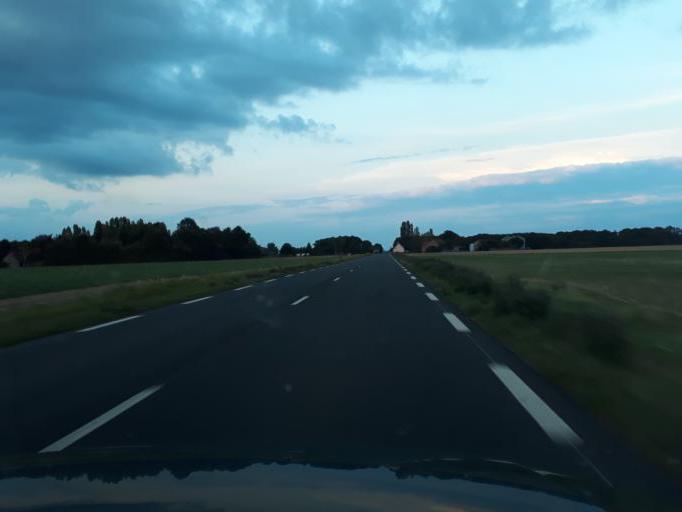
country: FR
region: Centre
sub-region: Departement du Loir-et-Cher
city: La Ville-aux-Clercs
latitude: 47.8917
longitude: 1.0582
